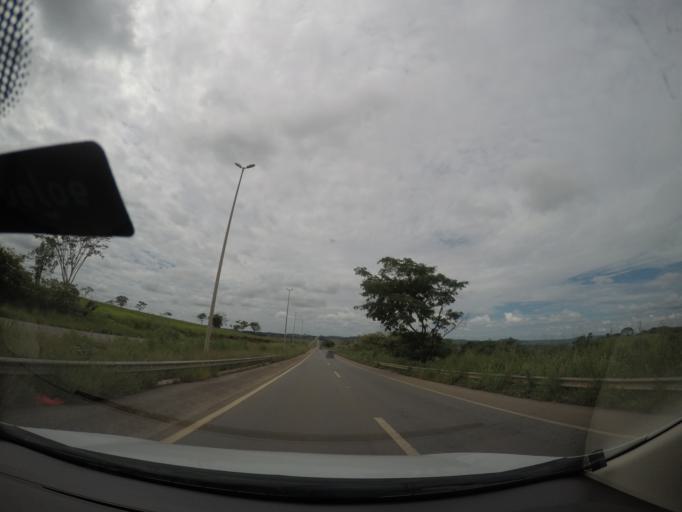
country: BR
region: Goias
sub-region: Inhumas
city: Inhumas
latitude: -16.4088
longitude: -49.4768
